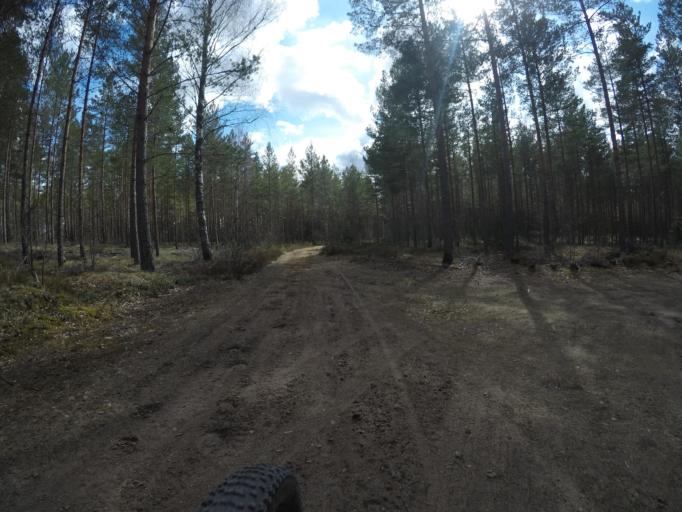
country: SE
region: Vaestmanland
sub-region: Kungsors Kommun
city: Kungsoer
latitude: 59.3514
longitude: 16.1077
